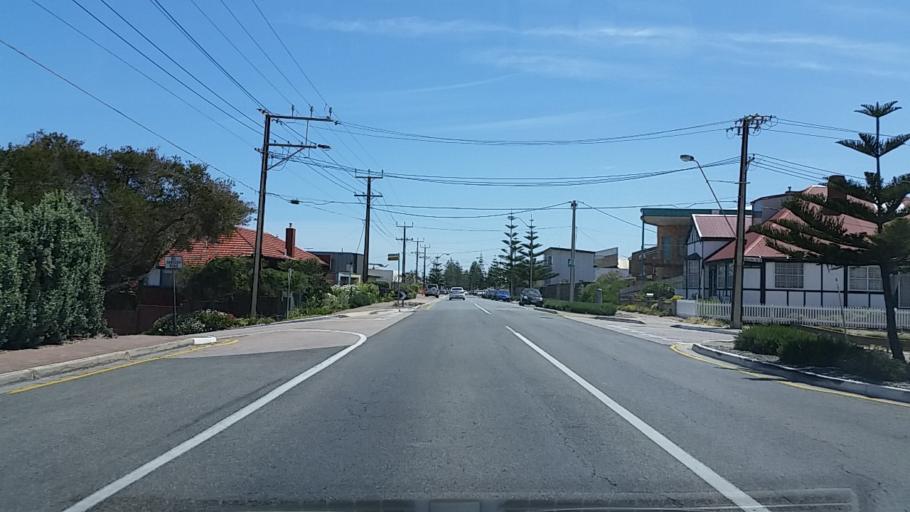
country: AU
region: South Australia
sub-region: Charles Sturt
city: Henley Beach
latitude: -34.9110
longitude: 138.4920
